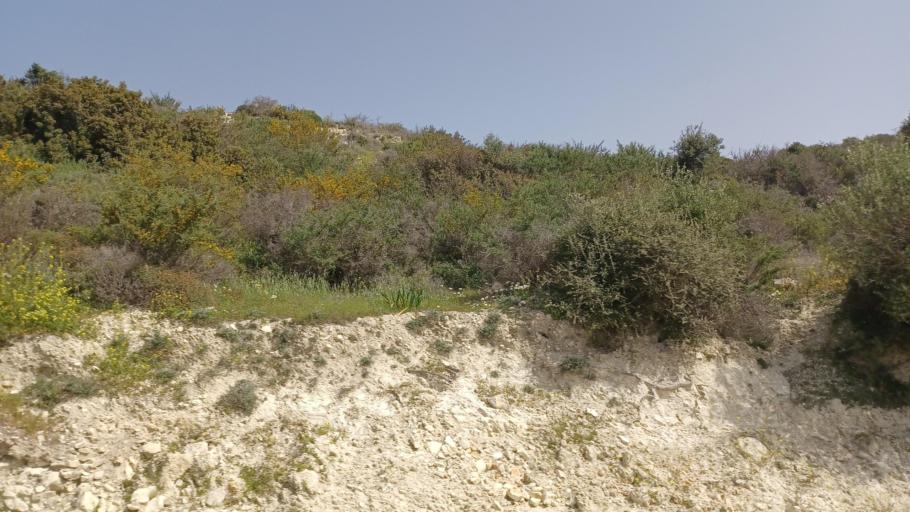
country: CY
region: Limassol
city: Pissouri
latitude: 34.7042
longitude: 32.7058
